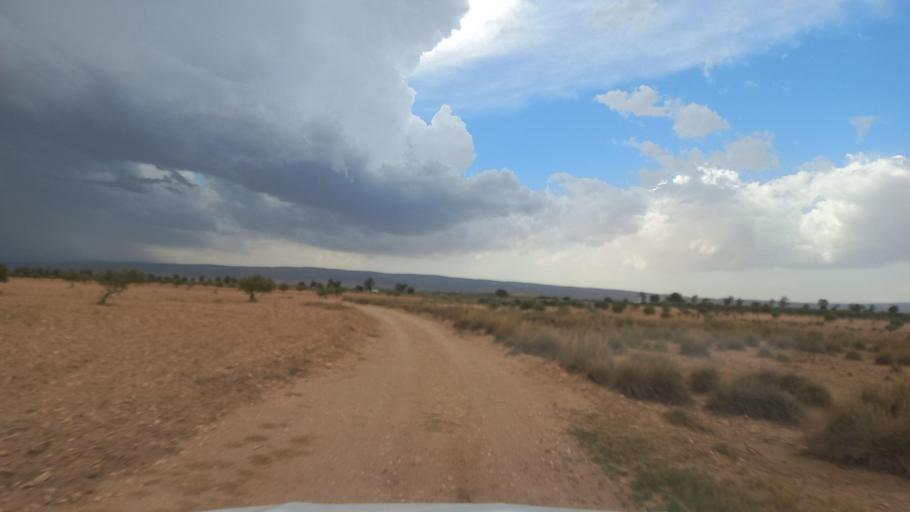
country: TN
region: Al Qasrayn
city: Kasserine
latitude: 35.2444
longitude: 9.0077
